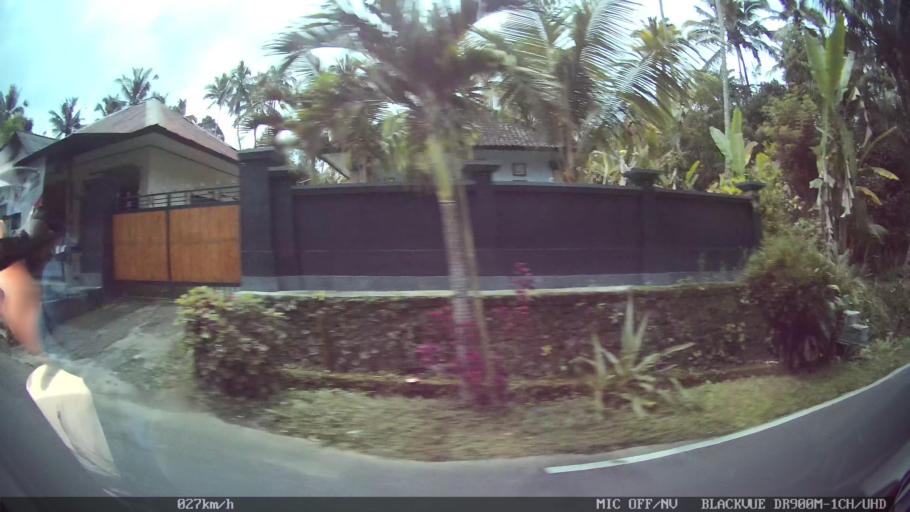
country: ID
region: Bali
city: Banjar Geriana Kangin
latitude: -8.4158
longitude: 115.4372
